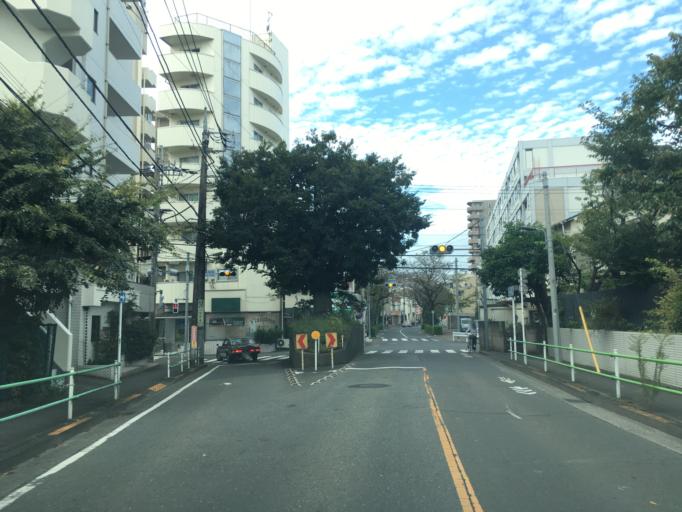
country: JP
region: Tokyo
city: Chofugaoka
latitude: 35.6437
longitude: 139.5392
